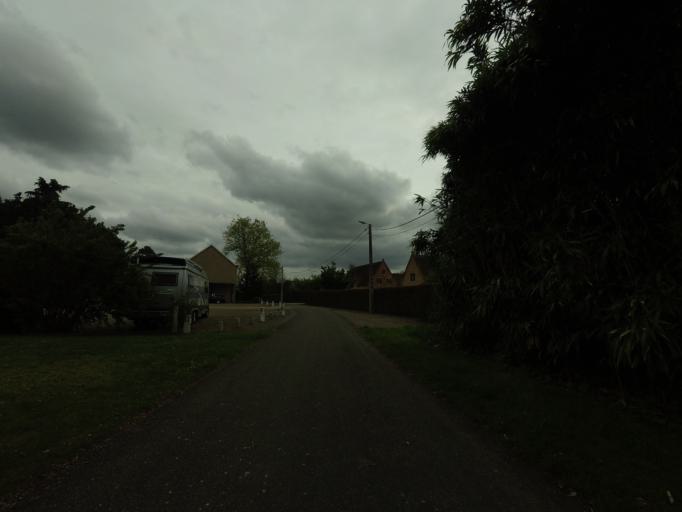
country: BE
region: Flanders
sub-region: Provincie Antwerpen
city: Mechelen
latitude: 51.0581
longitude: 4.4749
